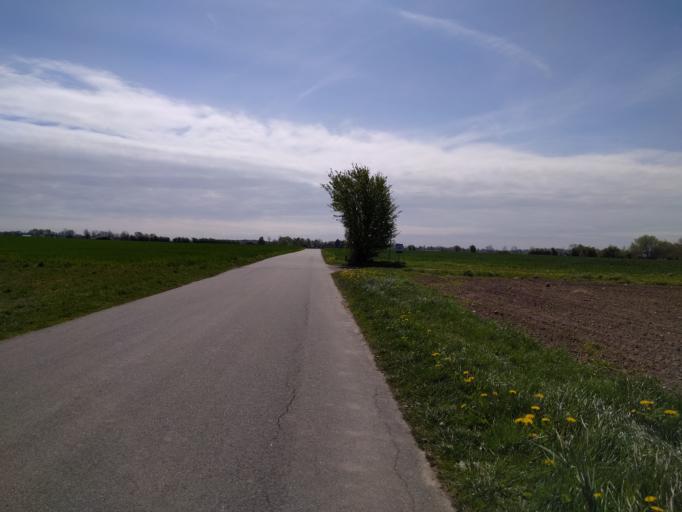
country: DK
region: South Denmark
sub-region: Kerteminde Kommune
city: Munkebo
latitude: 55.4432
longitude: 10.5893
